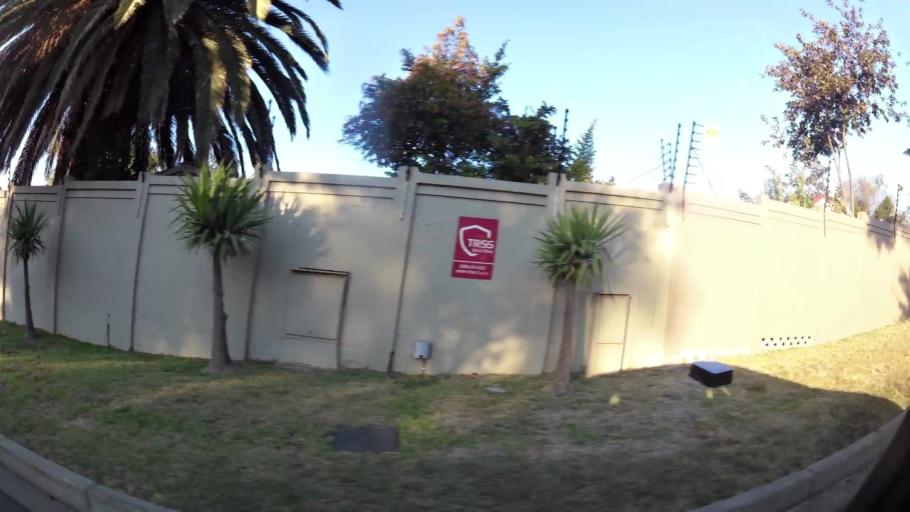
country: ZA
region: Gauteng
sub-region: City of Johannesburg Metropolitan Municipality
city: Diepsloot
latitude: -26.0499
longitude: 27.9770
